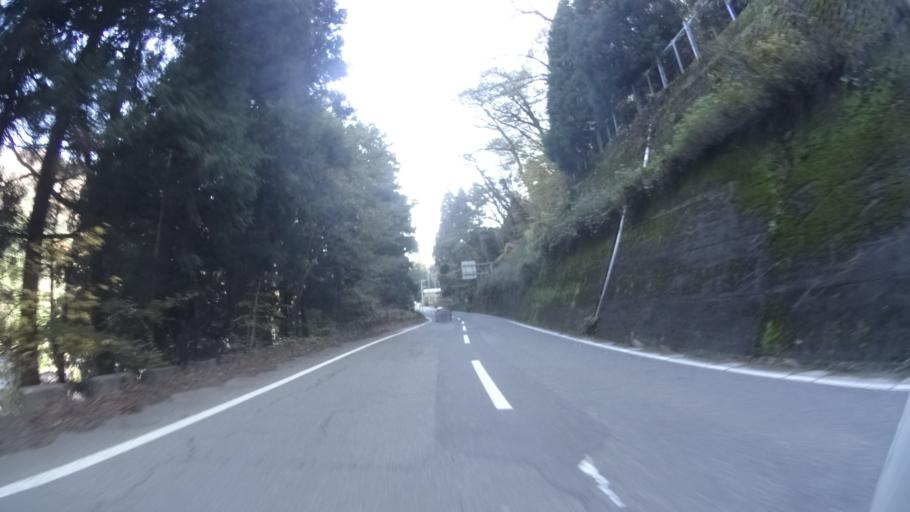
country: JP
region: Fukui
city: Ono
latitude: 35.9677
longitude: 136.5940
